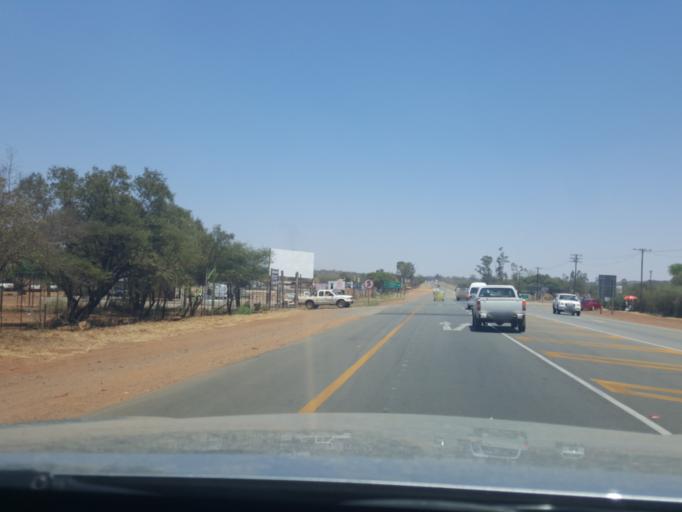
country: ZA
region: North-West
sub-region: Ngaka Modiri Molema District Municipality
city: Zeerust
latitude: -25.5594
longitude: 26.0639
